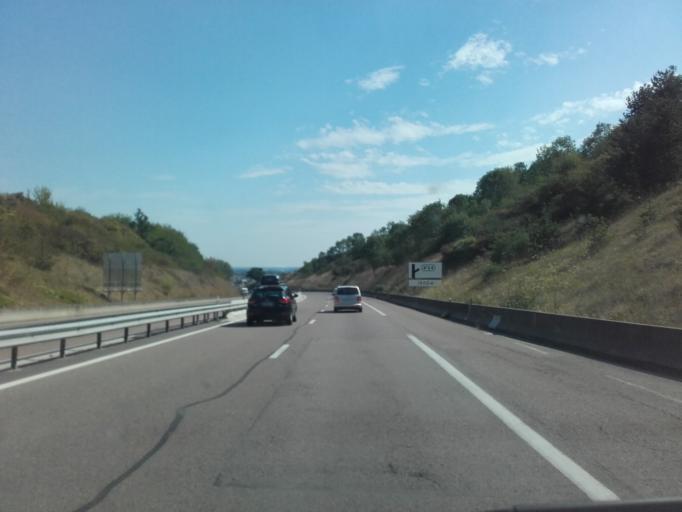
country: FR
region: Bourgogne
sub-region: Departement de la Cote-d'Or
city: Savigny-les-Beaune
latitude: 47.0521
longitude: 4.8301
